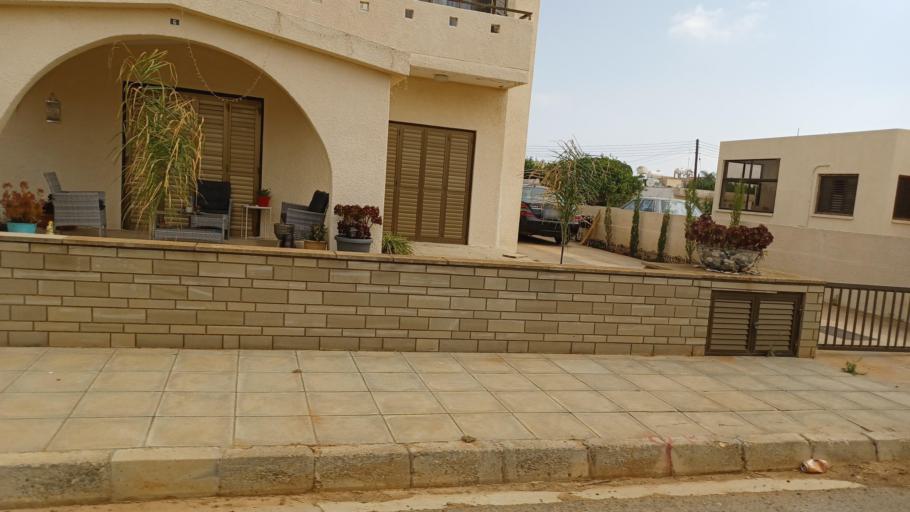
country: CY
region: Ammochostos
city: Deryneia
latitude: 35.0547
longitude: 33.9560
